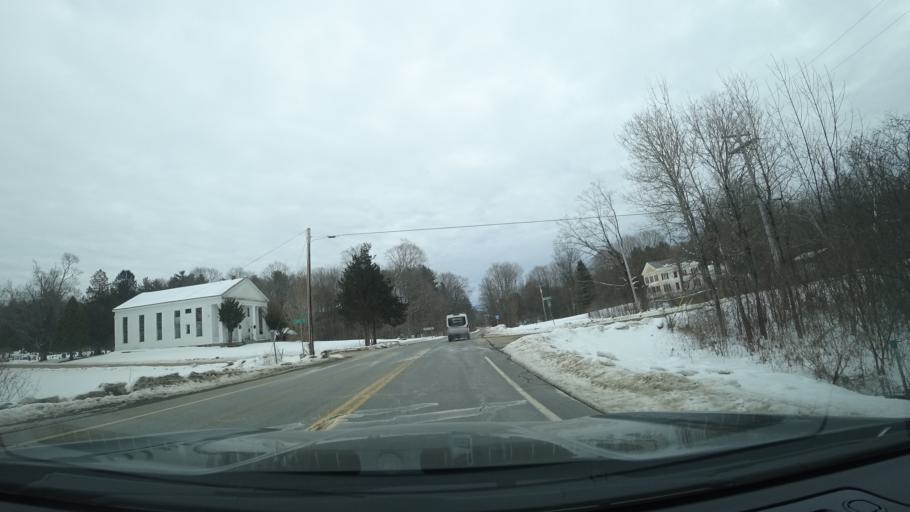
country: US
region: New York
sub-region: Washington County
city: Greenwich
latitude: 43.1907
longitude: -73.4624
